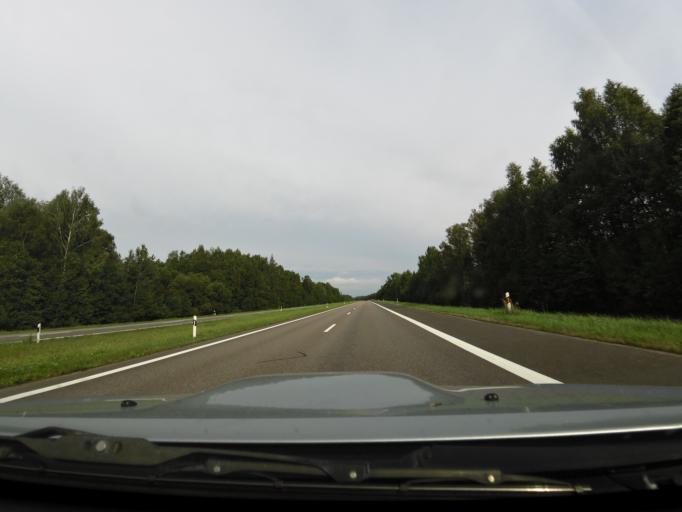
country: LT
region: Panevezys
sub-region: Panevezys City
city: Panevezys
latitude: 55.6353
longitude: 24.4000
